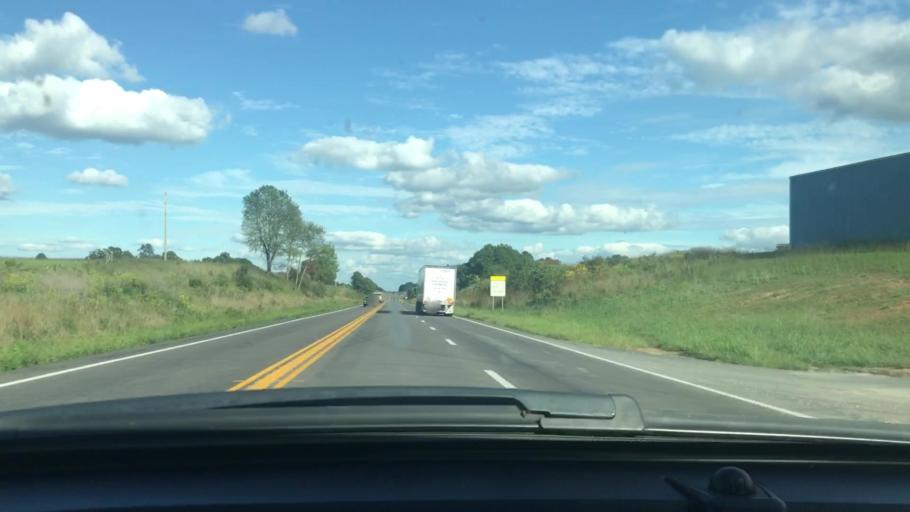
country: US
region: Missouri
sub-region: Oregon County
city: Thayer
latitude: 36.5878
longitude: -91.6335
